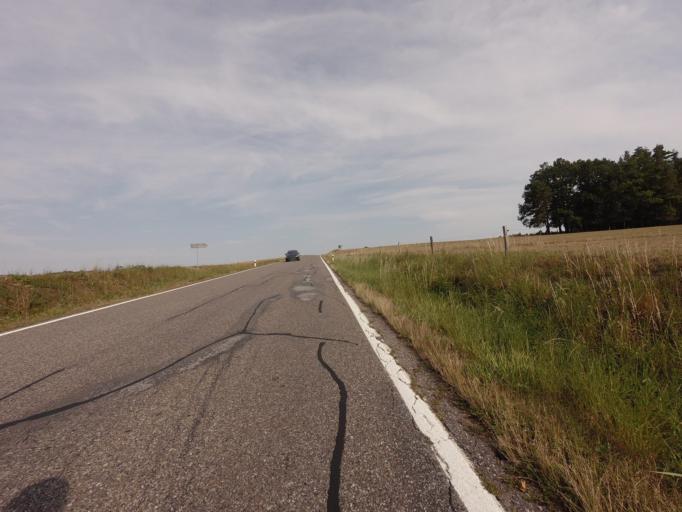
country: CZ
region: Jihocesky
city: Milevsko
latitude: 49.4836
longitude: 14.3668
